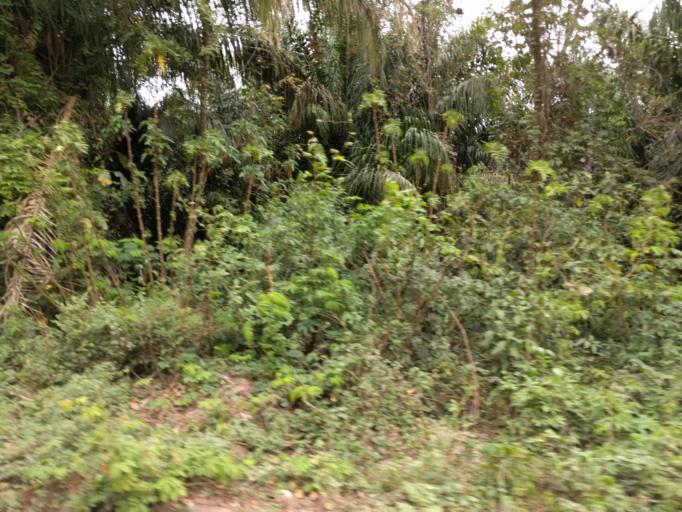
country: BO
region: Santa Cruz
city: Santiago del Torno
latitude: -17.9154
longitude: -63.4284
